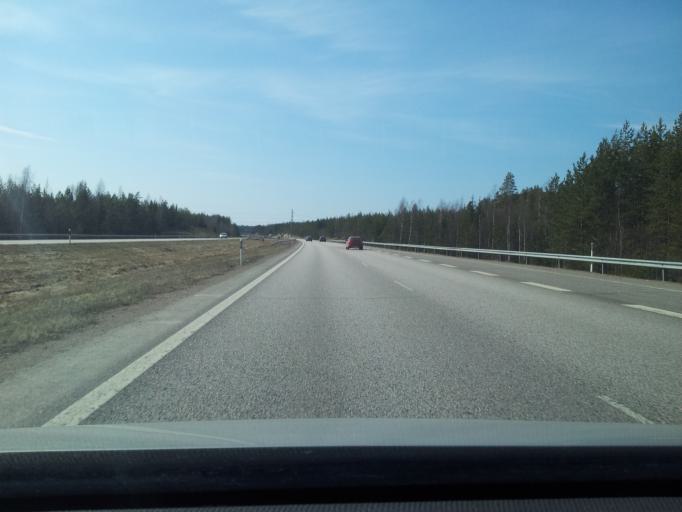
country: FI
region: Kymenlaakso
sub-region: Kotka-Hamina
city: Hamina
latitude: 60.5693
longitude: 27.0669
